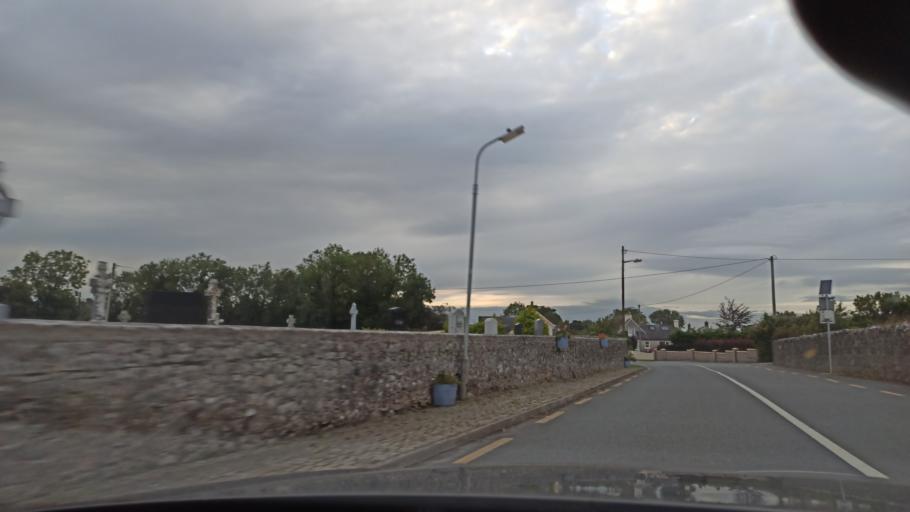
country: IE
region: Munster
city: Cashel
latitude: 52.4715
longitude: -7.8351
